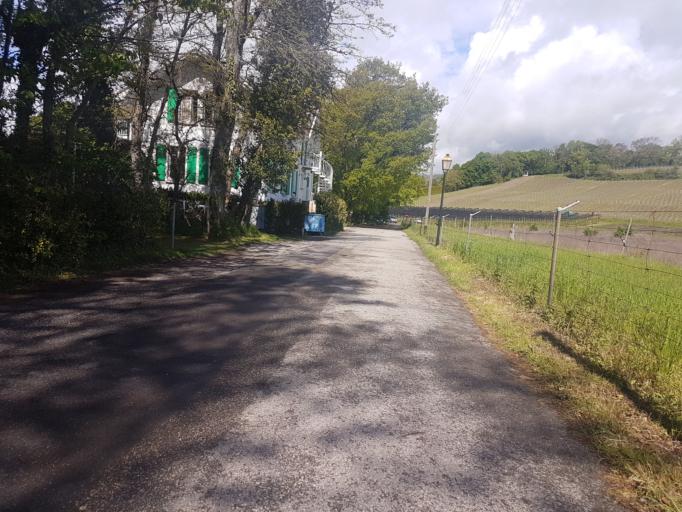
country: CH
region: Vaud
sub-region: Nyon District
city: Perroy
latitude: 46.4653
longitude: 6.3833
